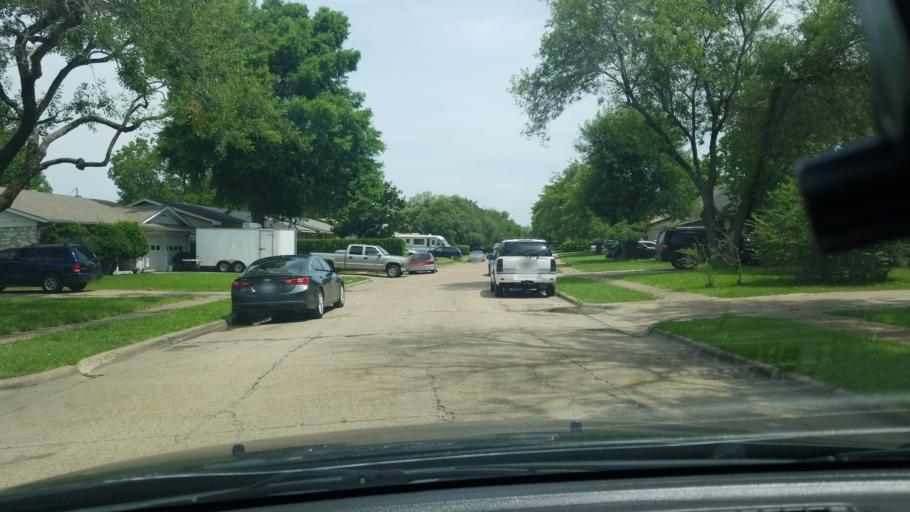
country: US
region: Texas
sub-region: Dallas County
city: Mesquite
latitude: 32.7568
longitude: -96.5801
